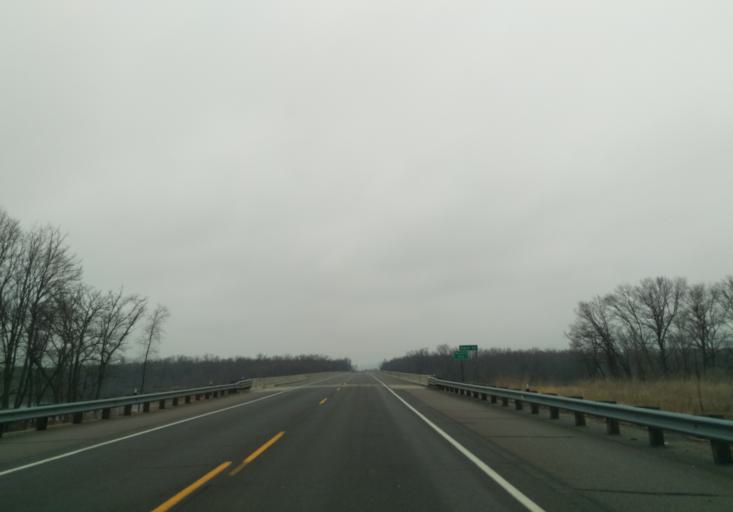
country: US
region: Wisconsin
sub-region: Sauk County
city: Spring Green
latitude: 43.1676
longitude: -90.0400
